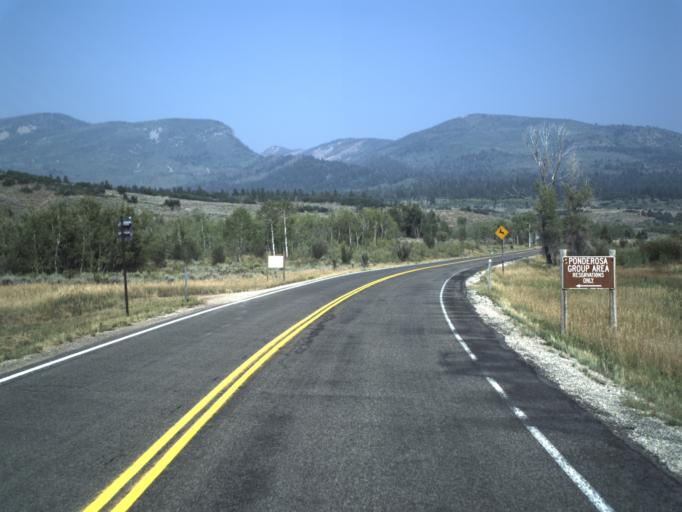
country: US
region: Utah
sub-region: Summit County
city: Kamas
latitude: 40.6306
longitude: -111.1946
